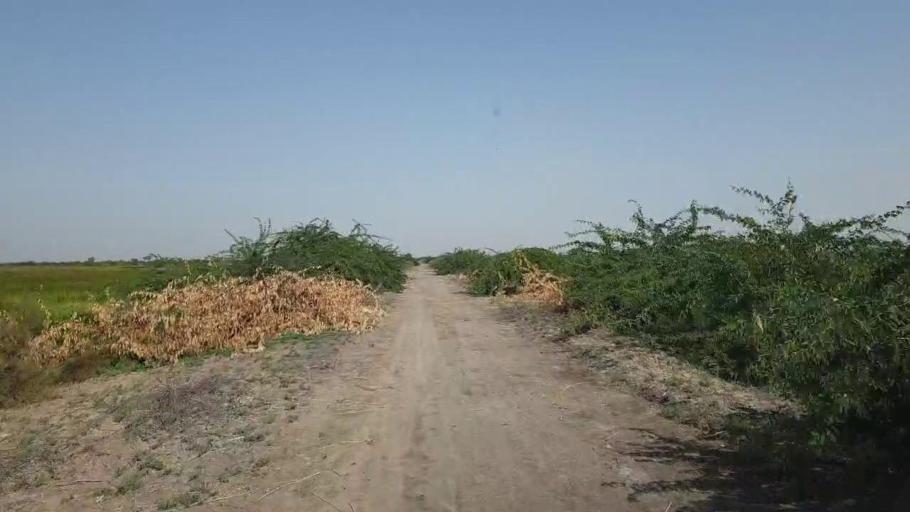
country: PK
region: Sindh
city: Tando Bago
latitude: 24.7135
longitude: 69.0720
